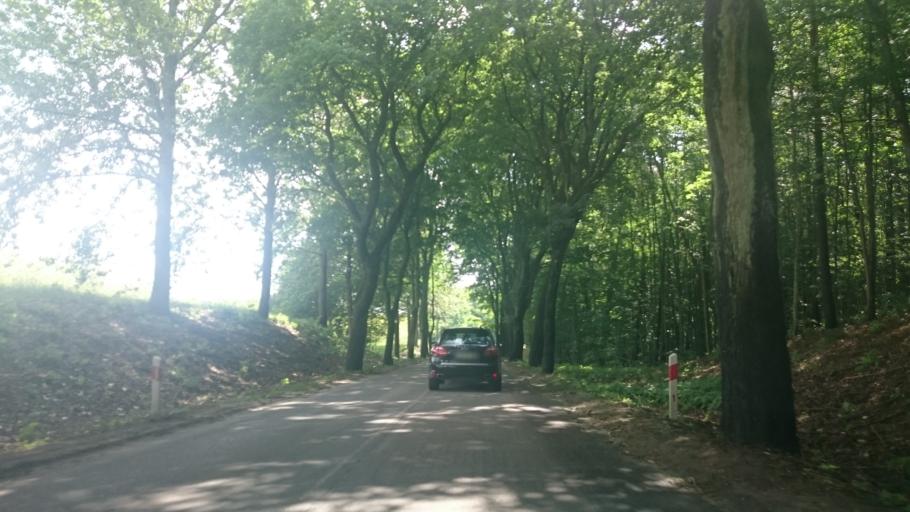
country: PL
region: Pomeranian Voivodeship
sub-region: Powiat starogardzki
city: Zblewo
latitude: 53.9680
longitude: 18.2782
